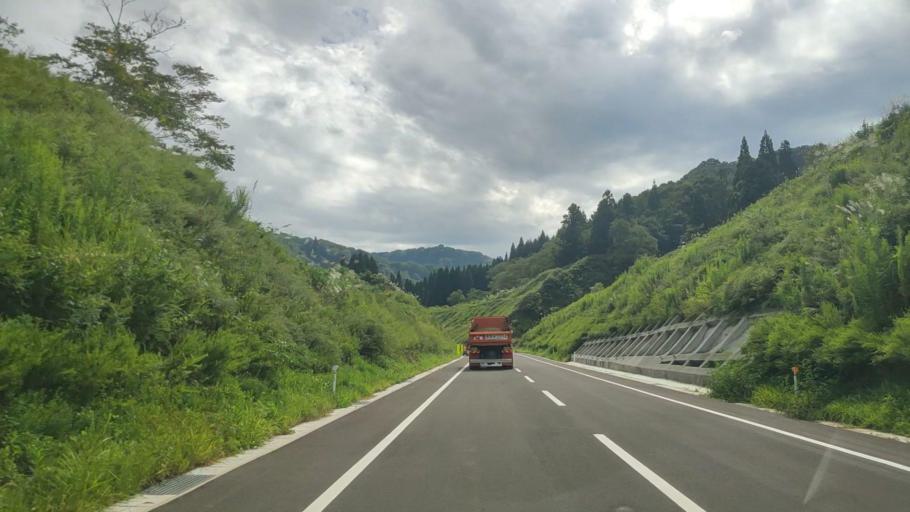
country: JP
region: Niigata
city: Arai
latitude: 36.9481
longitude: 138.2844
